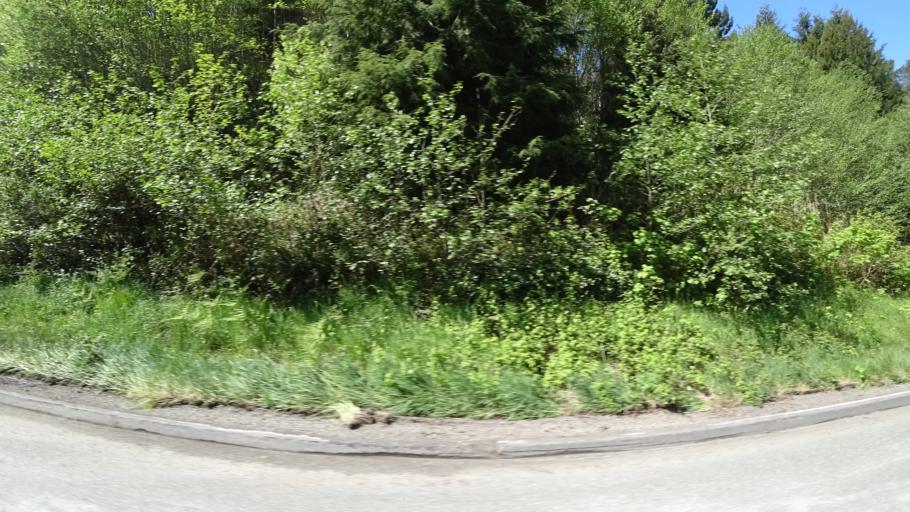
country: US
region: California
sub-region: Del Norte County
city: Bertsch-Oceanview
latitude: 41.4633
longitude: -124.0364
